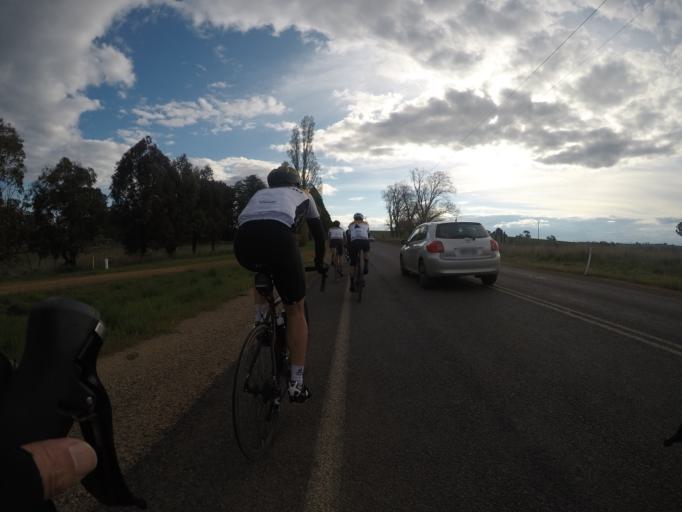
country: AU
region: New South Wales
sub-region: Orange Municipality
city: Orange
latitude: -33.2912
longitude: 149.0246
